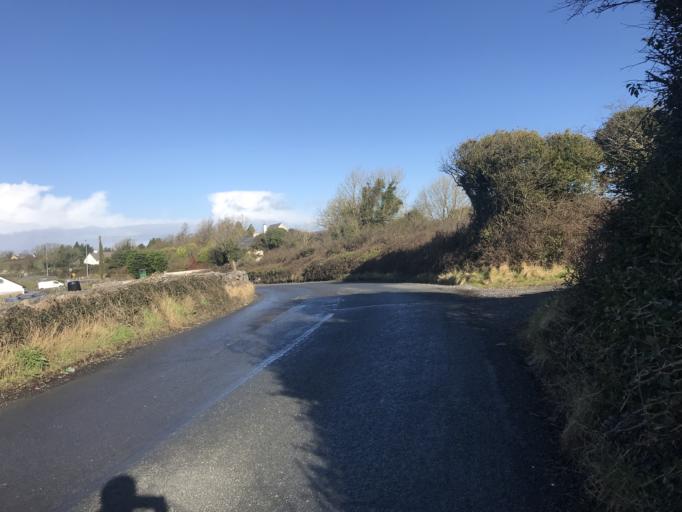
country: IE
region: Connaught
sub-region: County Galway
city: Gaillimh
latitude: 53.3116
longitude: -9.0220
